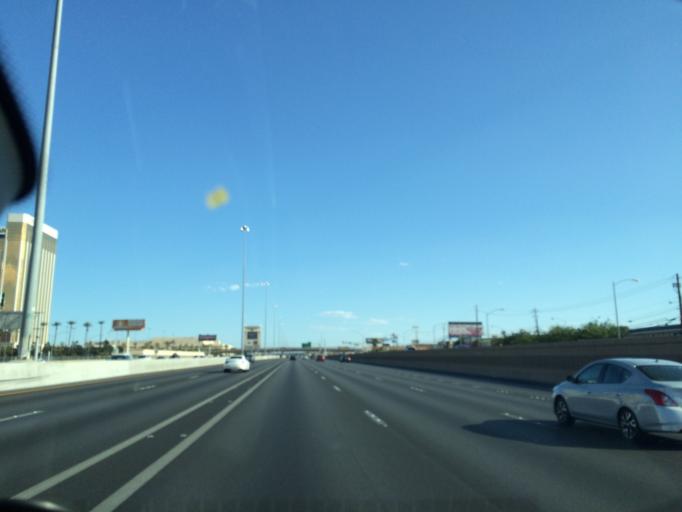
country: US
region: Nevada
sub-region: Clark County
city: Paradise
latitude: 36.0992
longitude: -115.1808
